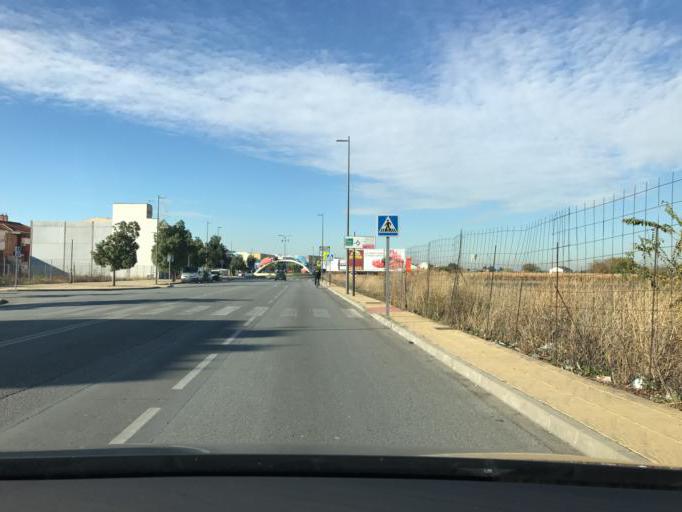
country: ES
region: Andalusia
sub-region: Provincia de Granada
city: Armilla
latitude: 37.1498
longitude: -3.6281
